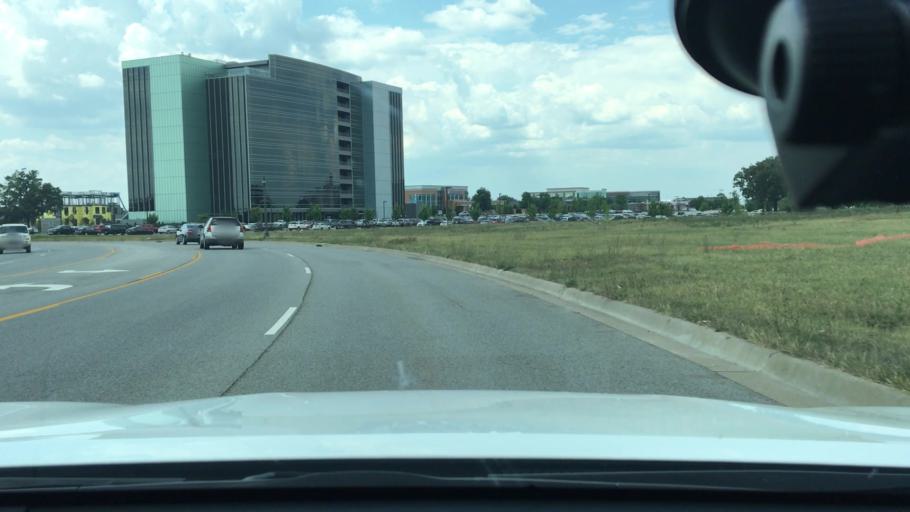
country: US
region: Arkansas
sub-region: Benton County
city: Cave Springs
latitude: 36.2998
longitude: -94.1869
